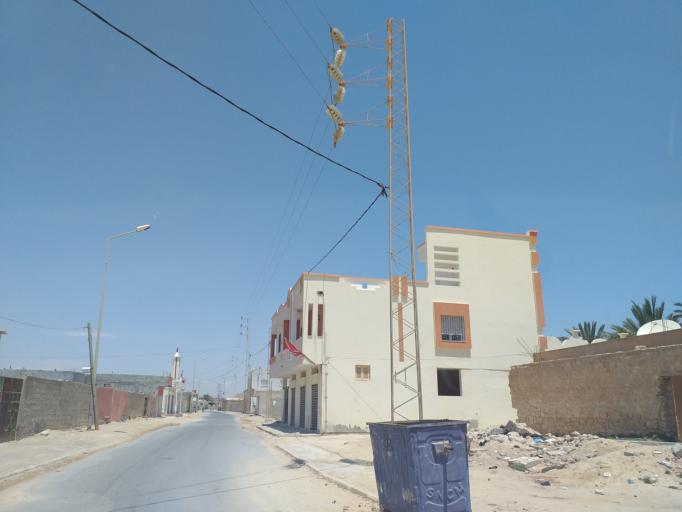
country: TN
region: Qabis
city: Gabes
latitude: 33.9433
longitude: 10.0598
